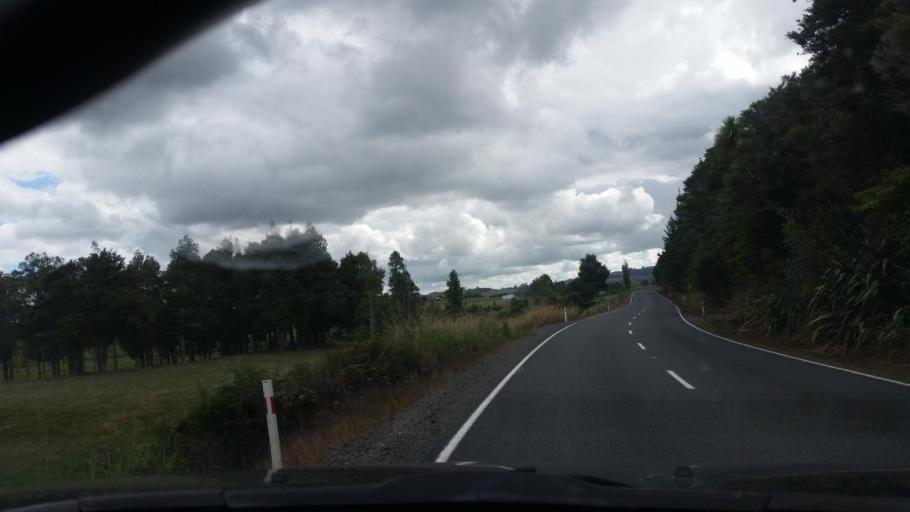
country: NZ
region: Northland
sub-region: Whangarei
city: Ruakaka
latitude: -35.9743
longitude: 174.2883
